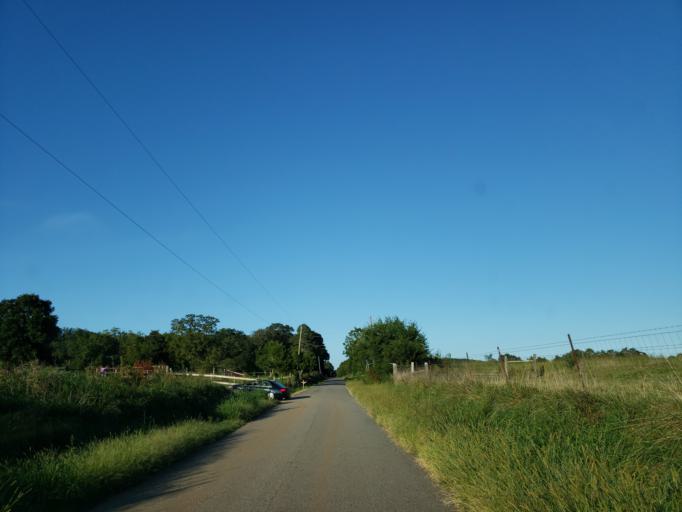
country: US
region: Georgia
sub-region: Bartow County
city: Rydal
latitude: 34.3300
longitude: -84.7237
